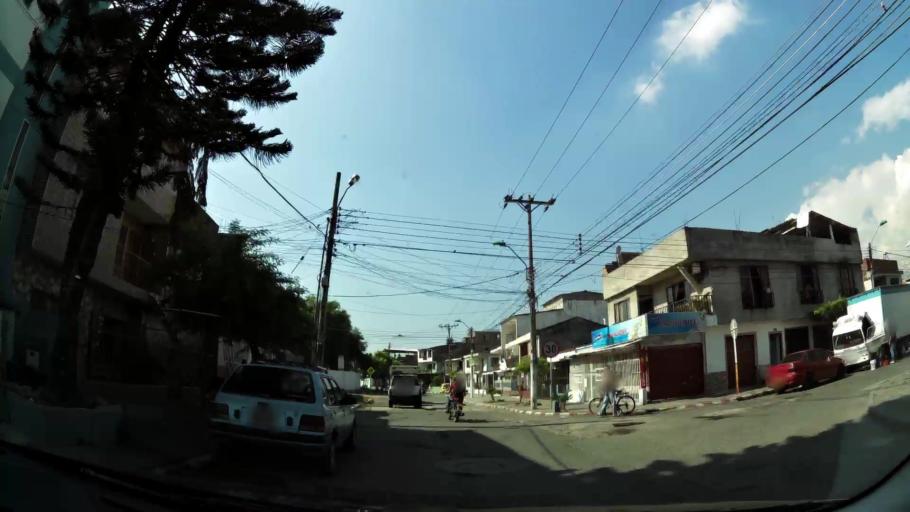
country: CO
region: Valle del Cauca
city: Cali
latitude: 3.4215
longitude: -76.5190
